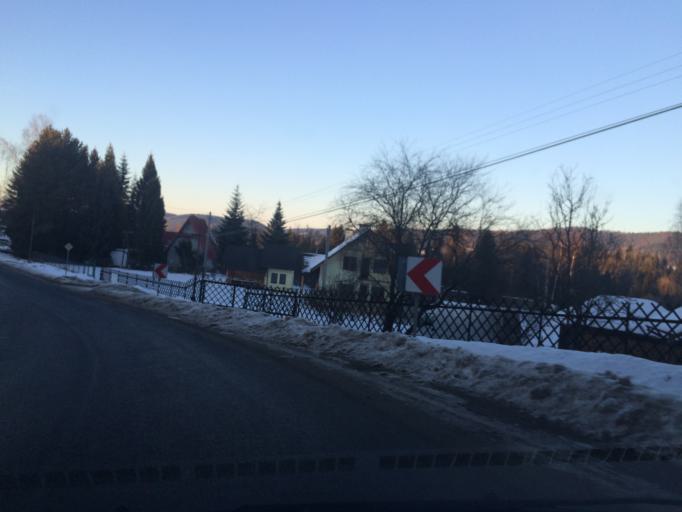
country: PL
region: Subcarpathian Voivodeship
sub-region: Powiat bieszczadzki
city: Czarna
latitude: 49.3099
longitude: 22.6732
